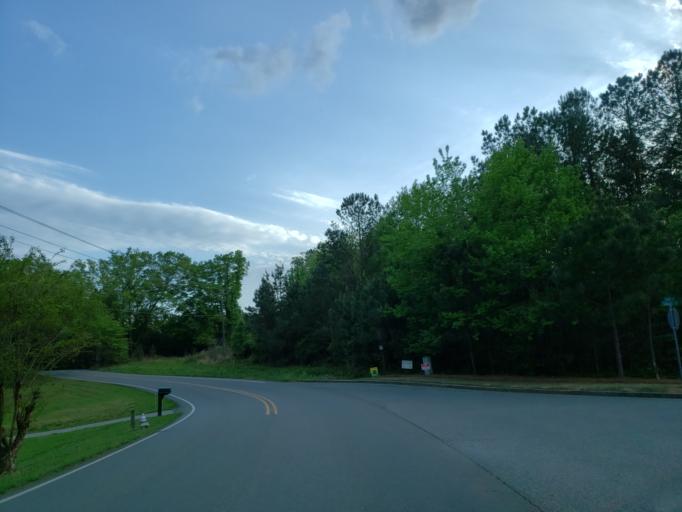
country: US
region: Georgia
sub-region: Cherokee County
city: Canton
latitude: 34.2913
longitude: -84.4533
